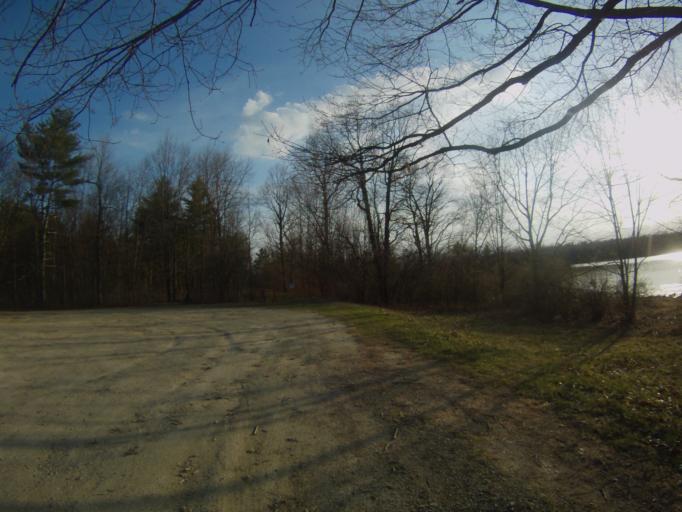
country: US
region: New York
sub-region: Essex County
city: Port Henry
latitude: 44.0731
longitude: -73.3480
